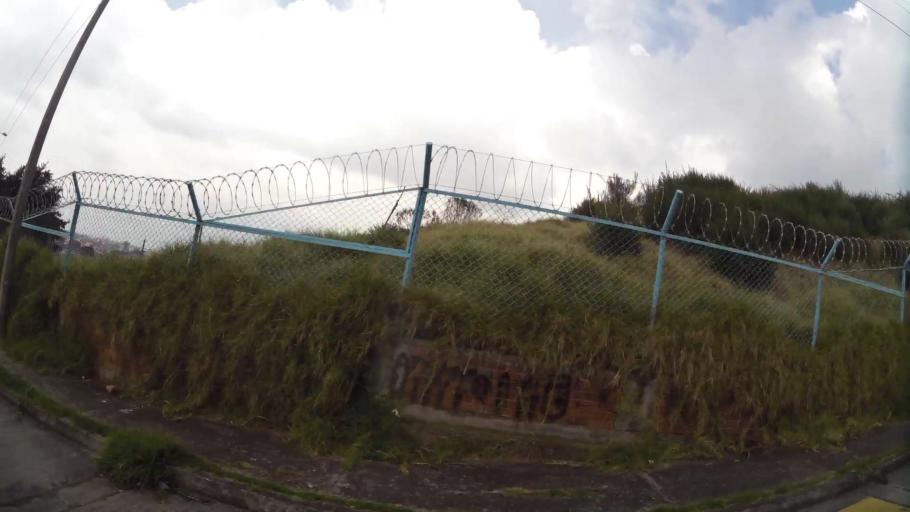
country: CO
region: Bogota D.C.
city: Bogota
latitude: 4.5748
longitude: -74.1199
